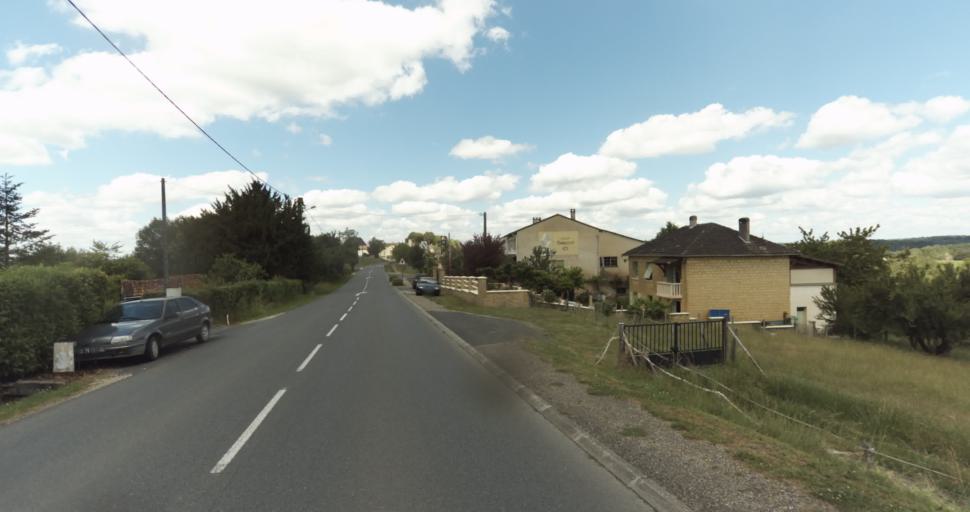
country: FR
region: Aquitaine
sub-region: Departement de la Dordogne
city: Beaumont-du-Perigord
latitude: 44.7633
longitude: 0.7698
